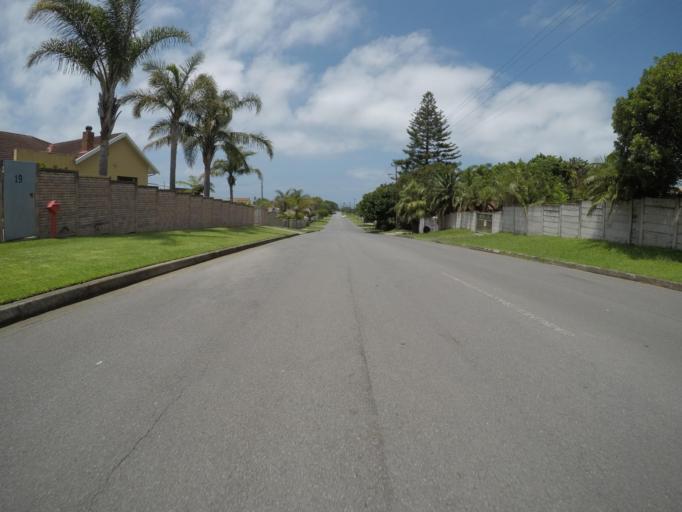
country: ZA
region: Eastern Cape
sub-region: Buffalo City Metropolitan Municipality
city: East London
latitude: -32.9421
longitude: 28.0100
